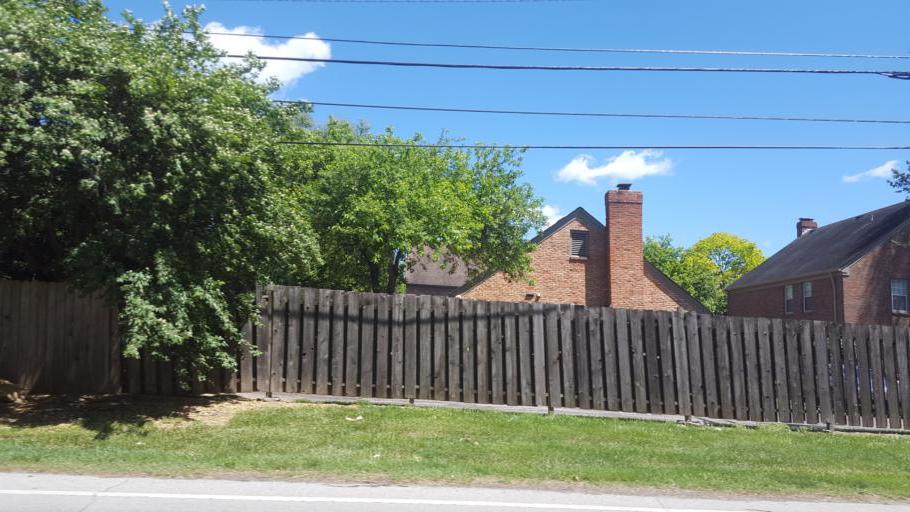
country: US
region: Ohio
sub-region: Franklin County
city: Dublin
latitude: 40.0448
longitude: -83.0945
